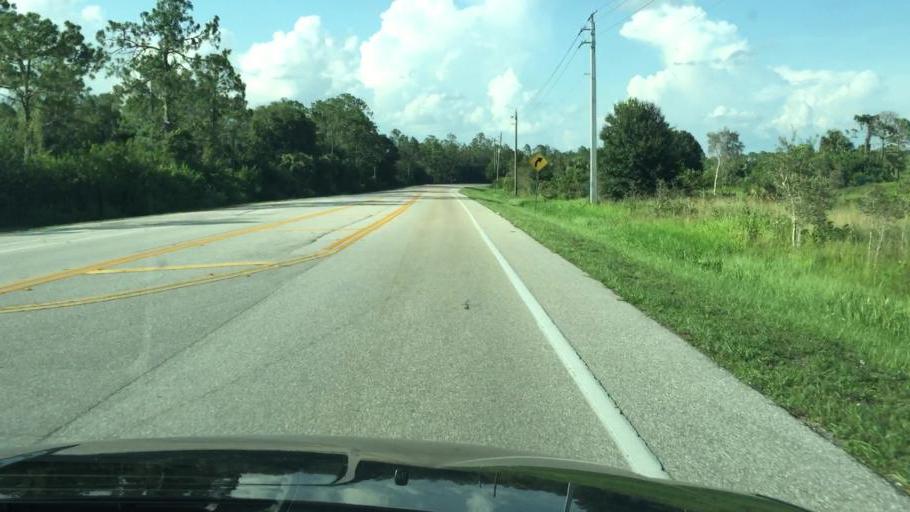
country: US
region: Florida
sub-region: Lee County
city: Buckingham
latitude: 26.6315
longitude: -81.7561
